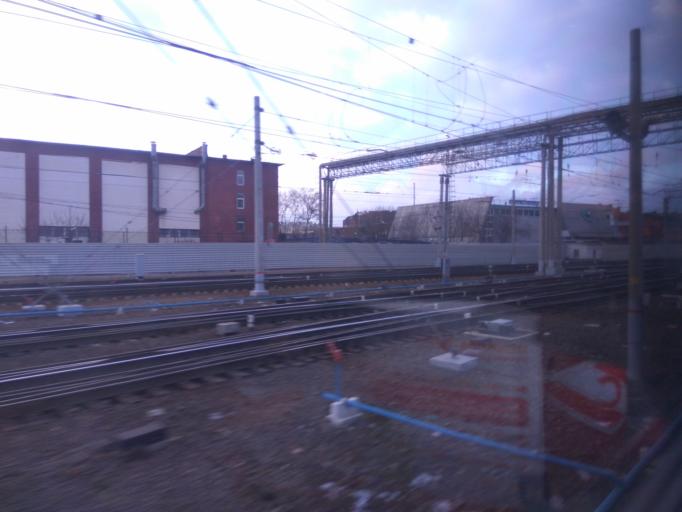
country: RU
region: St.-Petersburg
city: Centralniy
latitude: 59.9218
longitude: 30.3650
